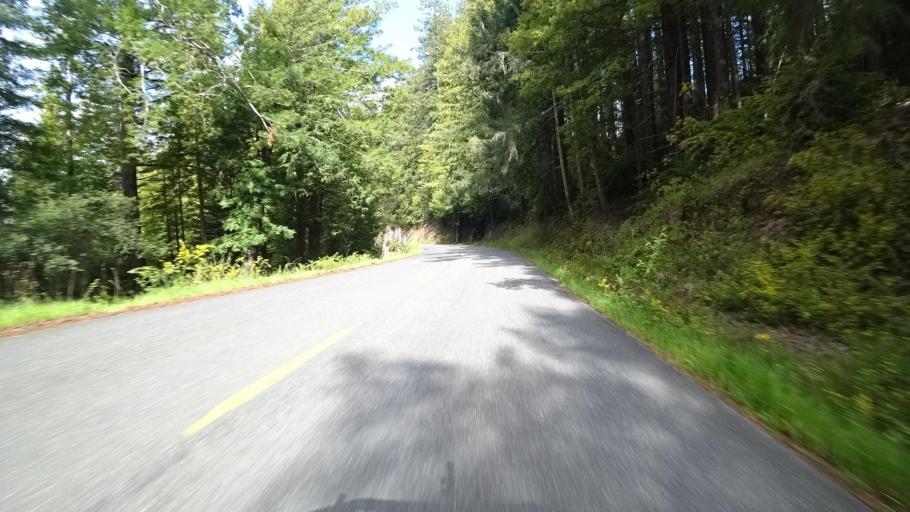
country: US
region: California
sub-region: Humboldt County
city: Bayside
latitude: 40.7564
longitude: -124.0345
